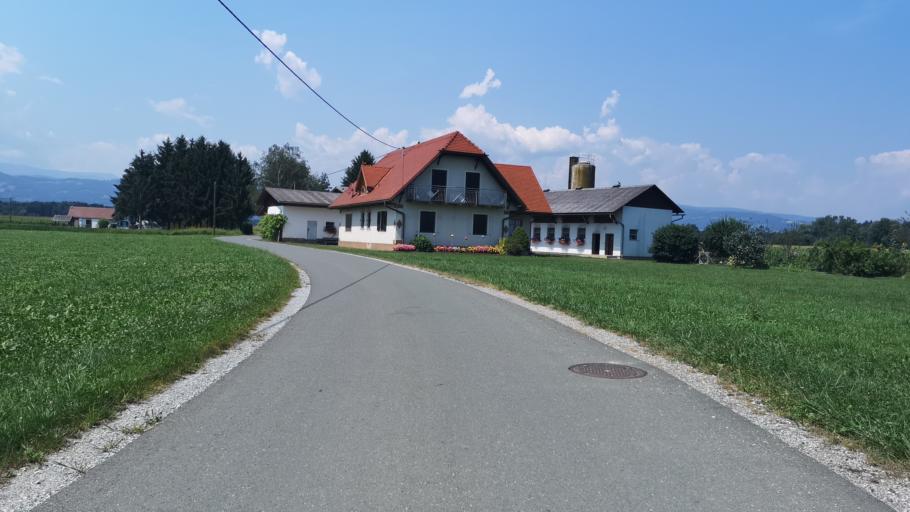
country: AT
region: Styria
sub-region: Politischer Bezirk Deutschlandsberg
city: Gross Sankt Florian
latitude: 46.8170
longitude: 15.3016
